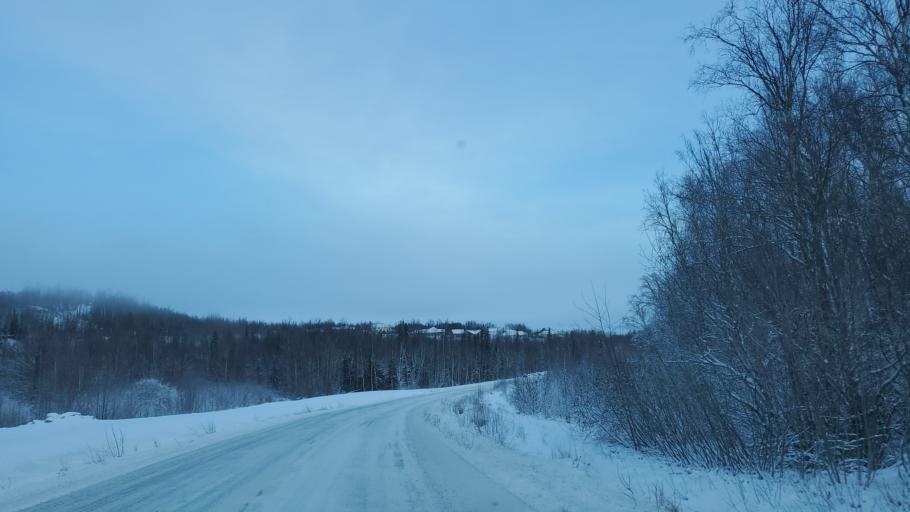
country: US
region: Alaska
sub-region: Matanuska-Susitna Borough
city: Lakes
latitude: 61.5505
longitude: -149.3022
